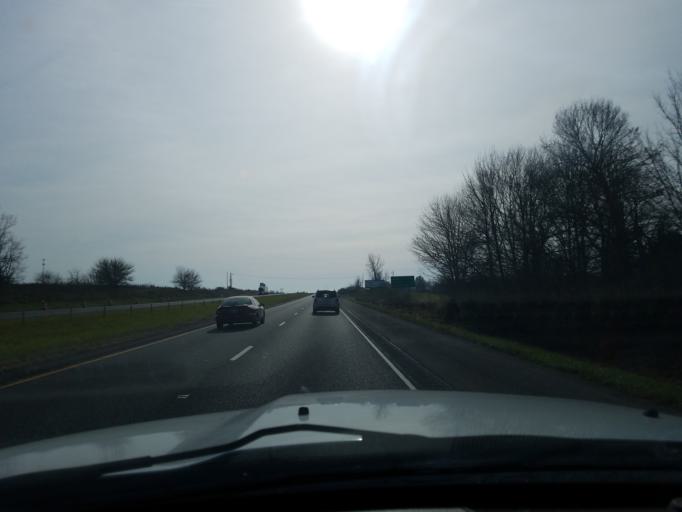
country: US
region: Indiana
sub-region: Delaware County
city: Yorktown
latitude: 40.2098
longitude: -85.5611
